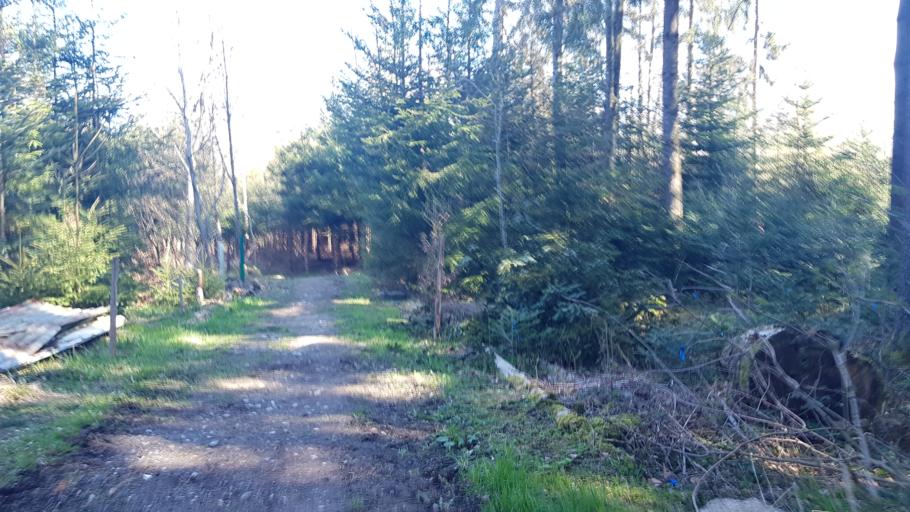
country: CH
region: Aargau
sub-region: Bezirk Kulm
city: Reinach
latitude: 47.2805
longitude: 8.1823
